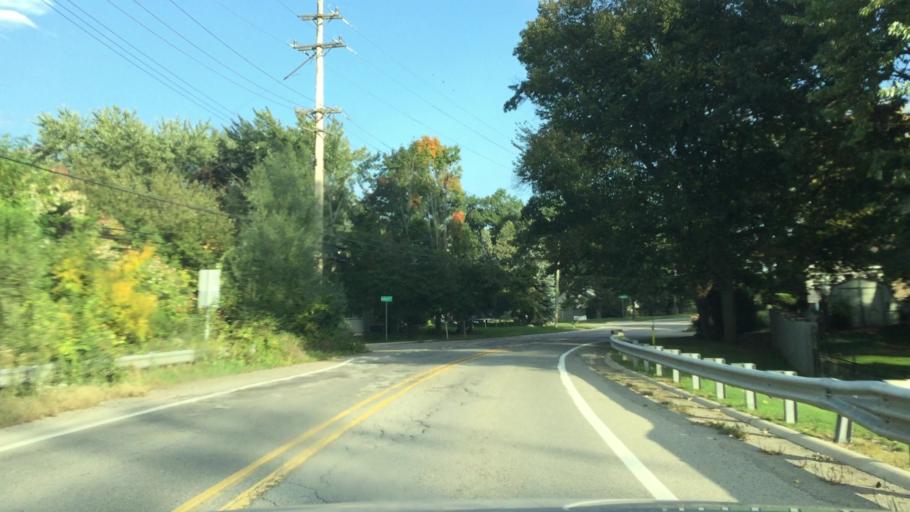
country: US
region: Michigan
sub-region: Oakland County
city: Wolverine Lake
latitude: 42.6409
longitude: -83.4820
